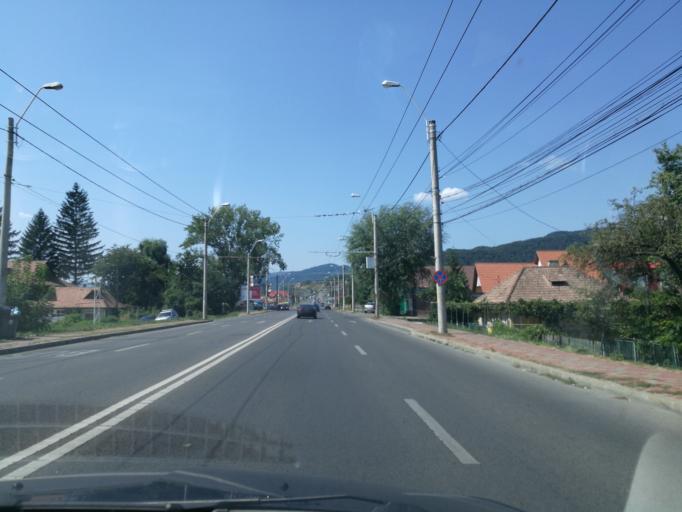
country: RO
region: Neamt
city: Piatra Neamt
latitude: 46.9380
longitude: 26.3418
